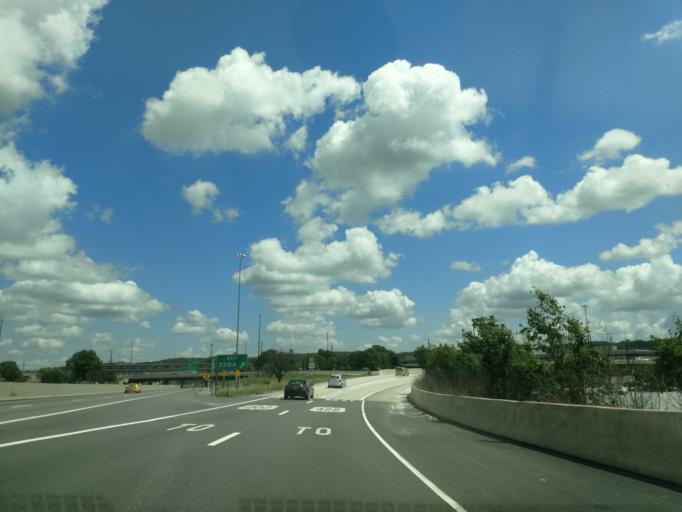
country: US
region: Pennsylvania
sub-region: Montgomery County
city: King of Prussia
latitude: 40.0851
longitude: -75.3983
